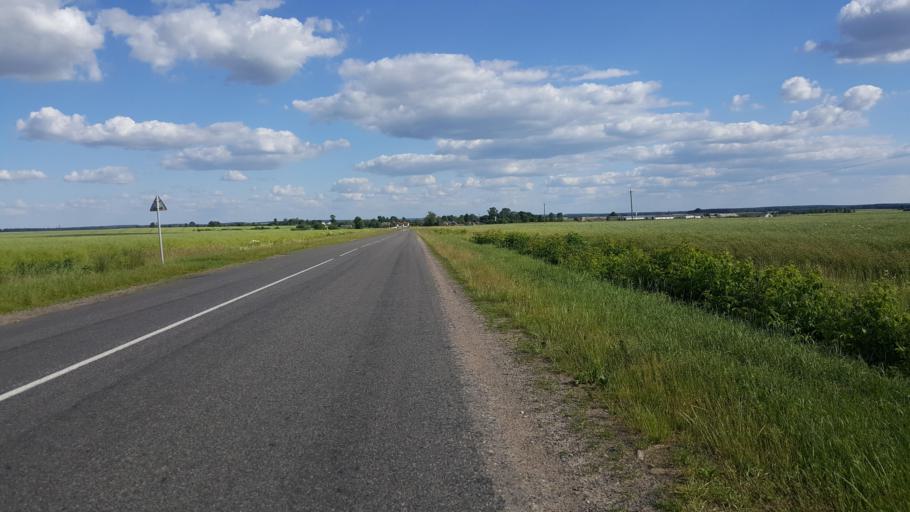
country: BY
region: Brest
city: Kamyanyets
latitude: 52.4402
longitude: 23.7435
